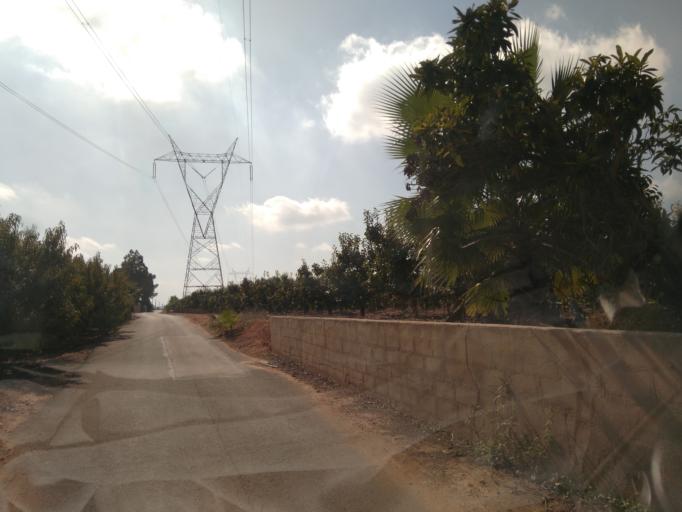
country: ES
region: Valencia
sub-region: Provincia de Valencia
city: Benimodo
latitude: 39.1809
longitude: -0.5508
